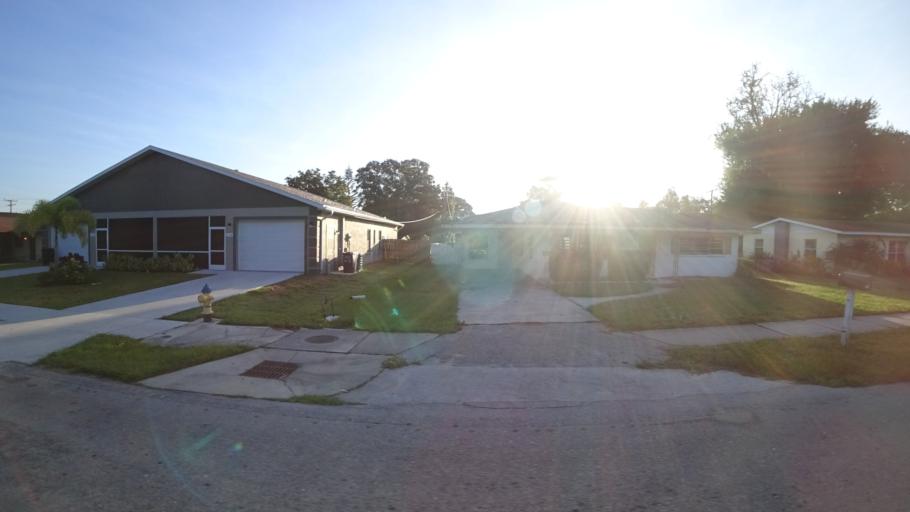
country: US
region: Florida
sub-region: Manatee County
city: South Bradenton
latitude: 27.4610
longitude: -82.5820
